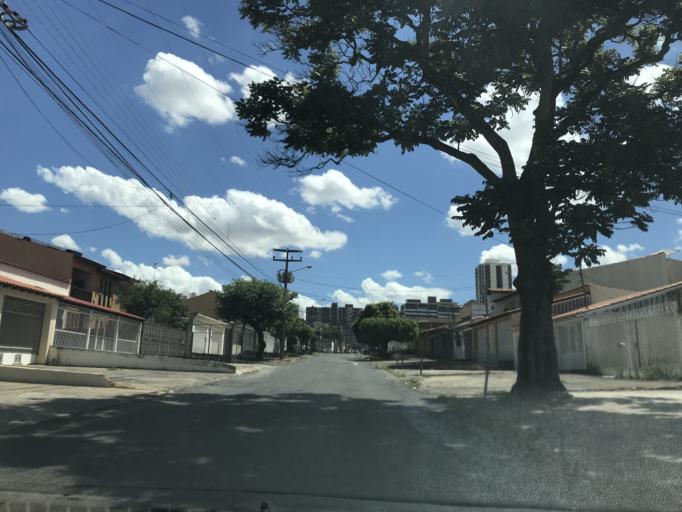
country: BR
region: Federal District
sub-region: Brasilia
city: Brasilia
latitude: -15.8386
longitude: -48.0602
